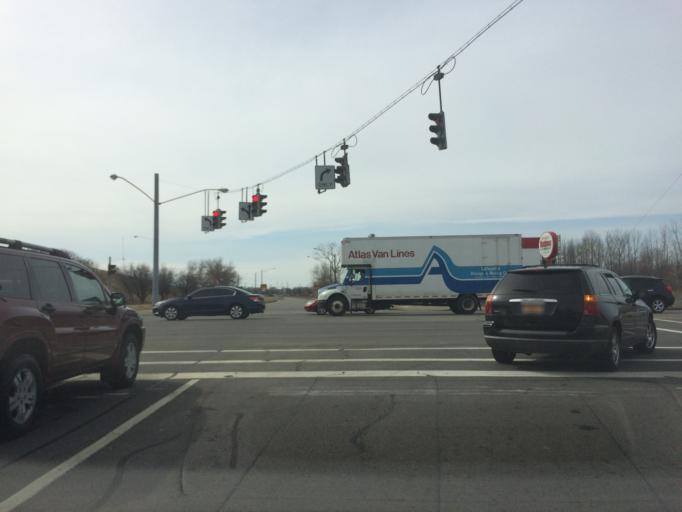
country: US
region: New York
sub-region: Monroe County
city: Rochester
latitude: 43.0884
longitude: -77.6358
